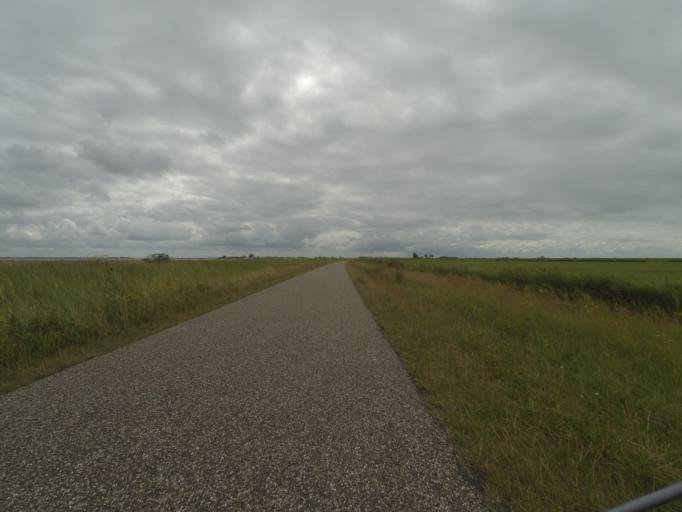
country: NL
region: Friesland
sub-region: Gemeente Dongeradeel
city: Anjum
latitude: 53.3992
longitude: 6.1524
